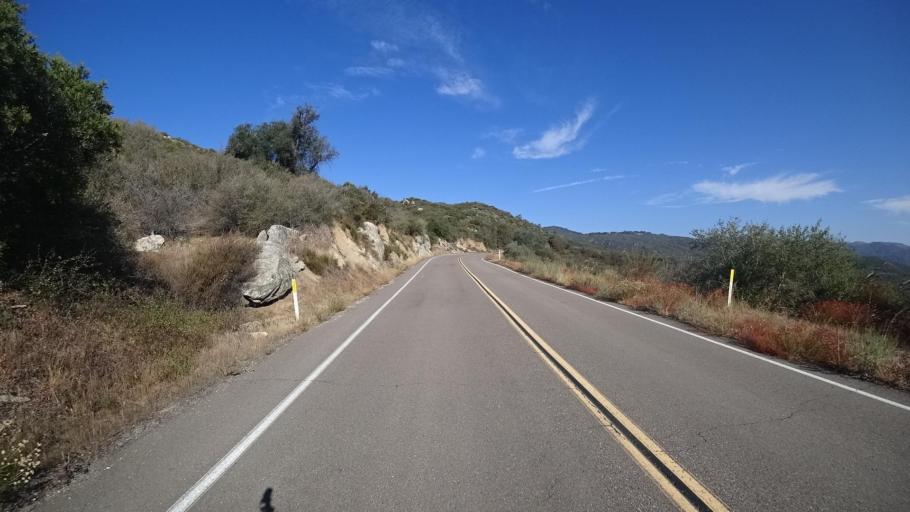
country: US
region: California
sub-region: Riverside County
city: Aguanga
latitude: 33.2566
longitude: -116.7616
